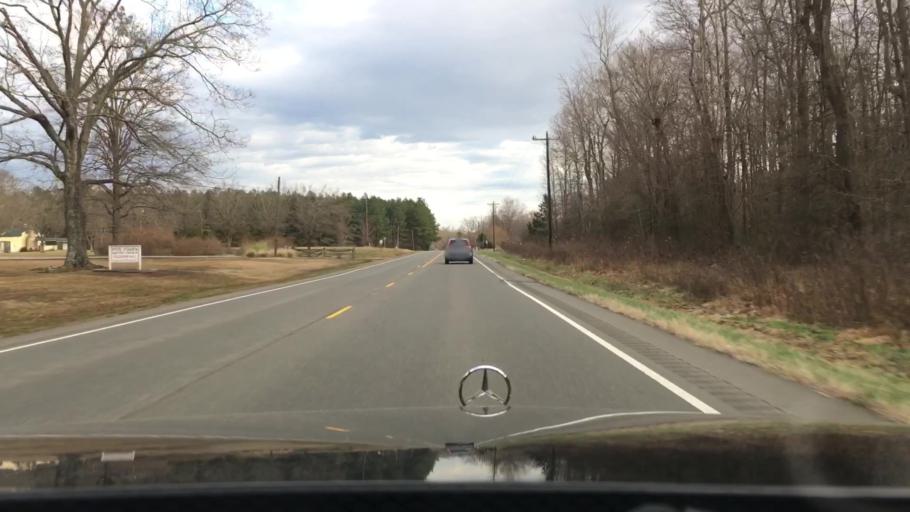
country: US
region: North Carolina
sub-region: Orange County
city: Hillsborough
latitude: 36.2052
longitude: -79.1525
